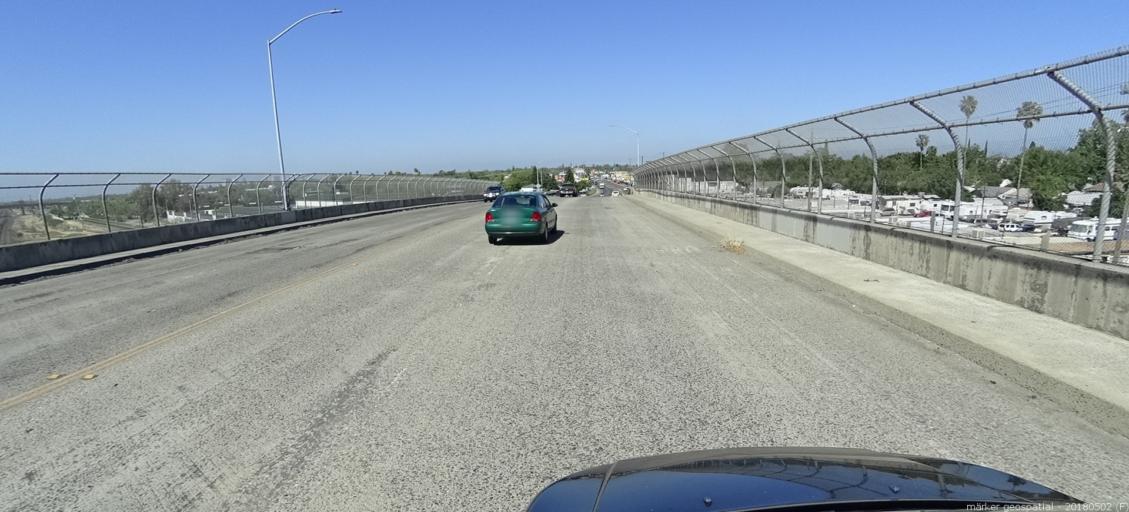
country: US
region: California
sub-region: Sacramento County
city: Arden-Arcade
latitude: 38.6109
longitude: -121.4354
